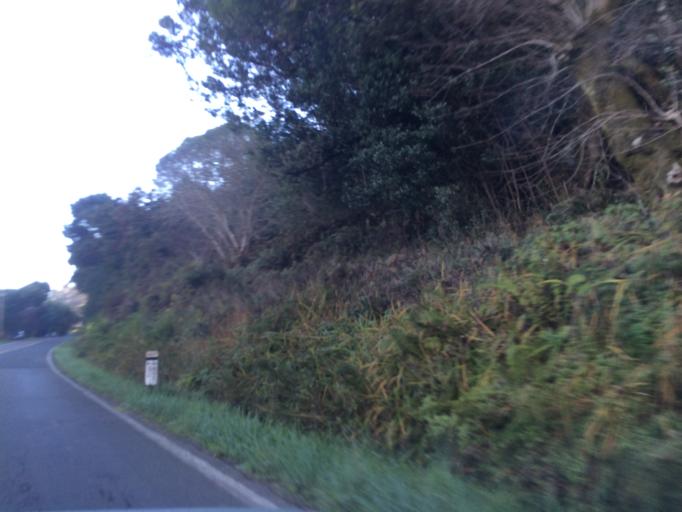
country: US
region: California
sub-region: Marin County
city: Inverness
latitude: 38.1090
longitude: -122.8649
